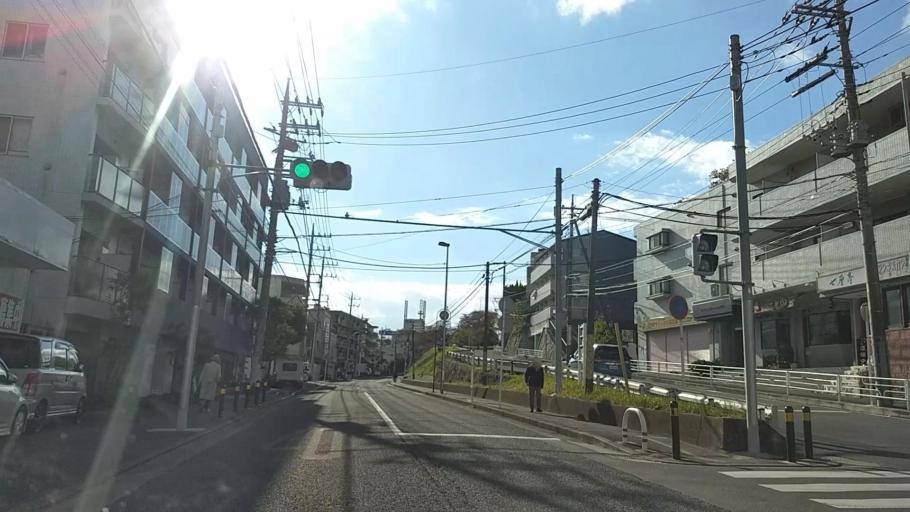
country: JP
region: Tokyo
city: Chofugaoka
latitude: 35.6117
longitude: 139.5205
